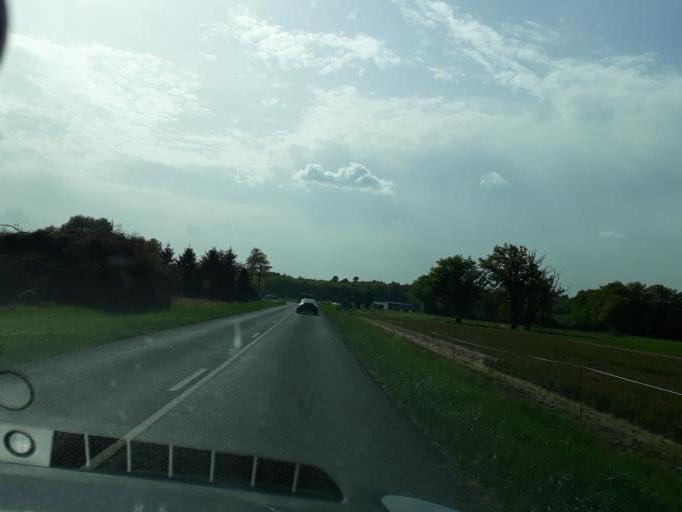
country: FR
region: Centre
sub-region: Departement du Loir-et-Cher
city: Saint-Laurent-Nouan
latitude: 47.6575
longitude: 1.6387
